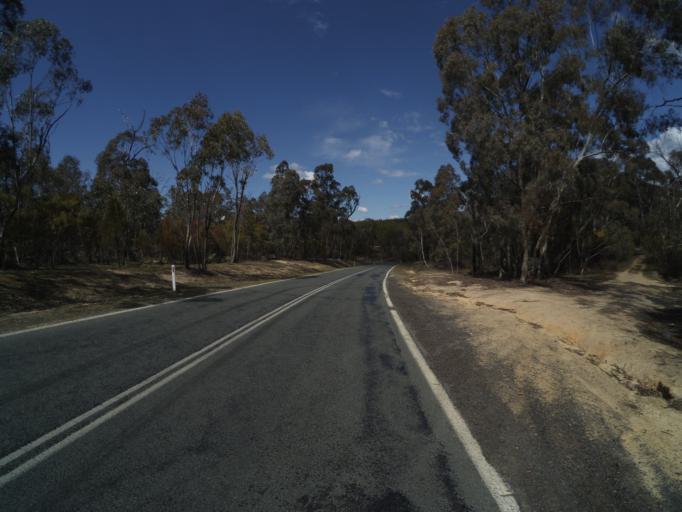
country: AU
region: Australian Capital Territory
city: Macquarie
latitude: -35.3522
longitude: 148.9406
